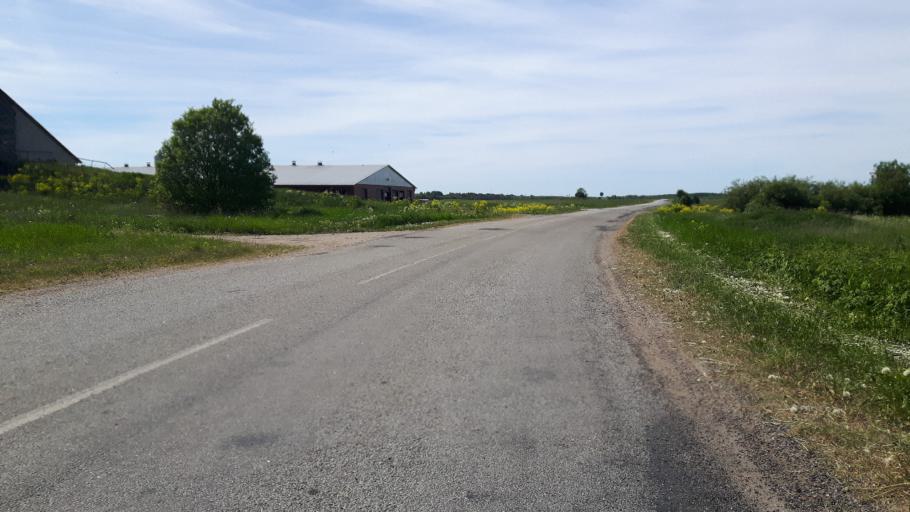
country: EE
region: Harju
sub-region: Kuusalu vald
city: Kuusalu
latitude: 59.4577
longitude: 25.3485
